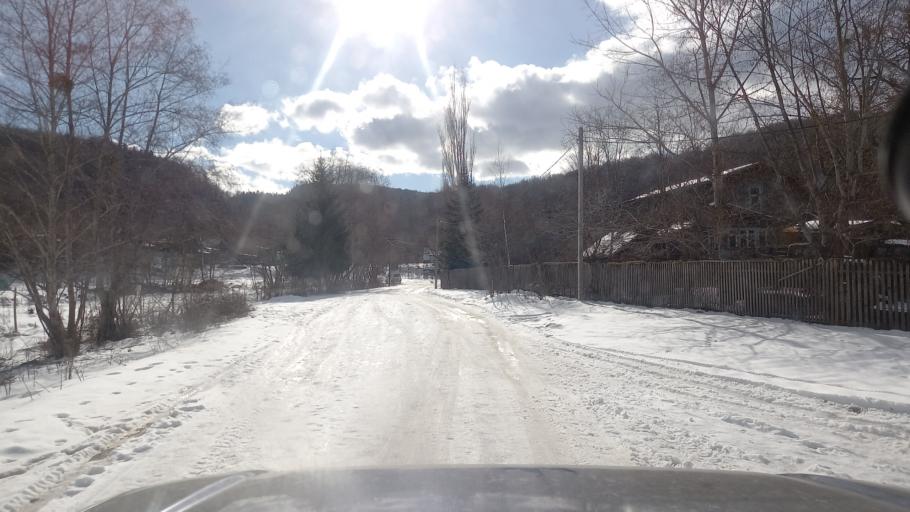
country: RU
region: Adygeya
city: Kamennomostskiy
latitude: 44.1942
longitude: 39.9607
